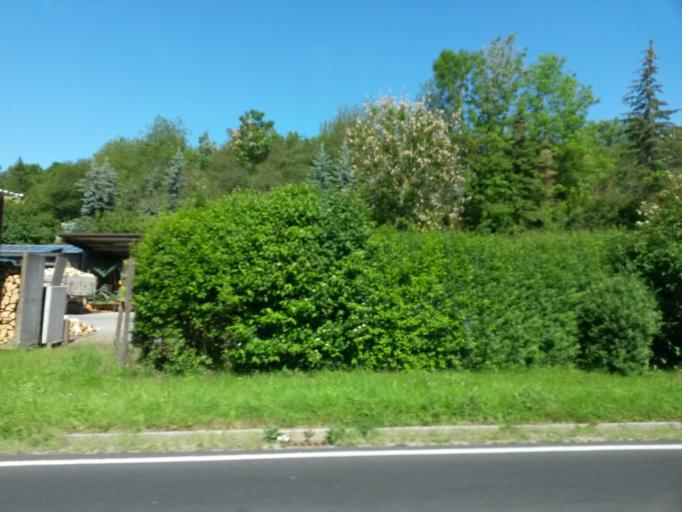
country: DE
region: Bavaria
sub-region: Regierungsbezirk Unterfranken
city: Wuerzburg
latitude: 49.8237
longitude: 9.9599
